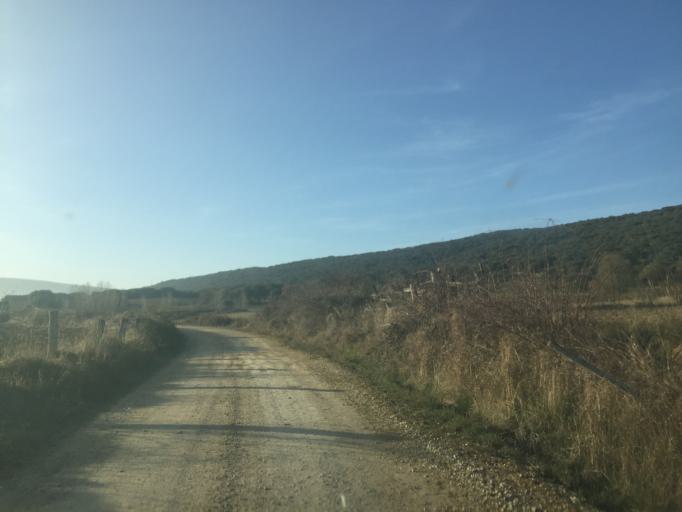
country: ES
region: Castille and Leon
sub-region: Provincia de Burgos
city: Medina de Pomar
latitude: 42.9274
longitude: -3.5938
